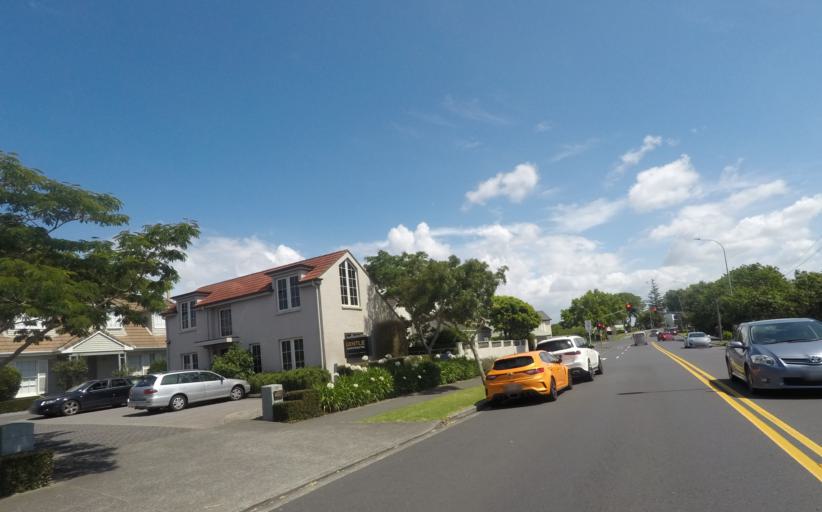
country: NZ
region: Auckland
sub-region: Auckland
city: Tamaki
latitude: -36.8742
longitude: 174.8286
